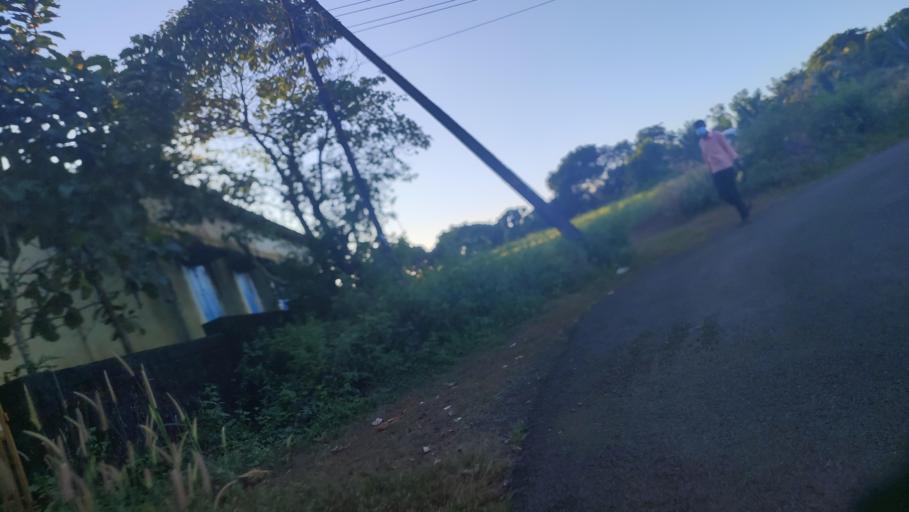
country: IN
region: Kerala
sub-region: Kasaragod District
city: Kannangad
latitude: 12.4011
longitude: 75.0600
